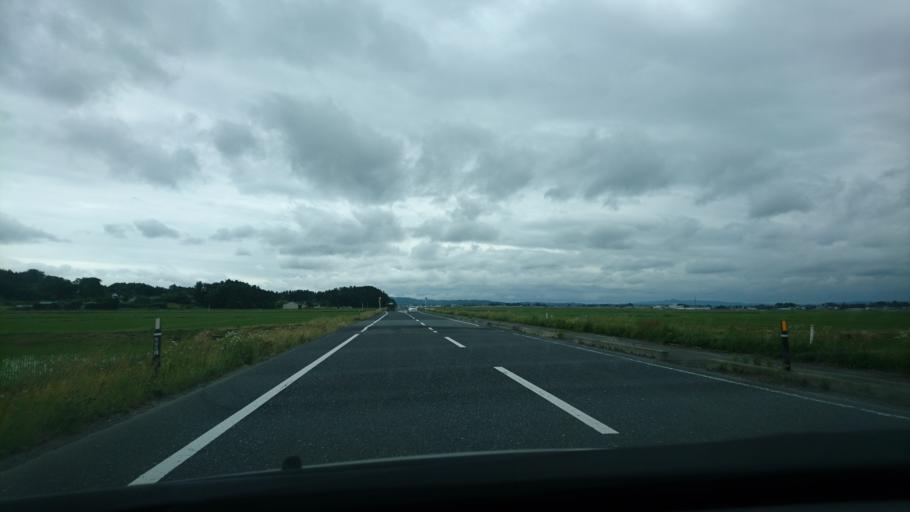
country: JP
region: Miyagi
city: Wakuya
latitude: 38.7018
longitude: 141.2602
